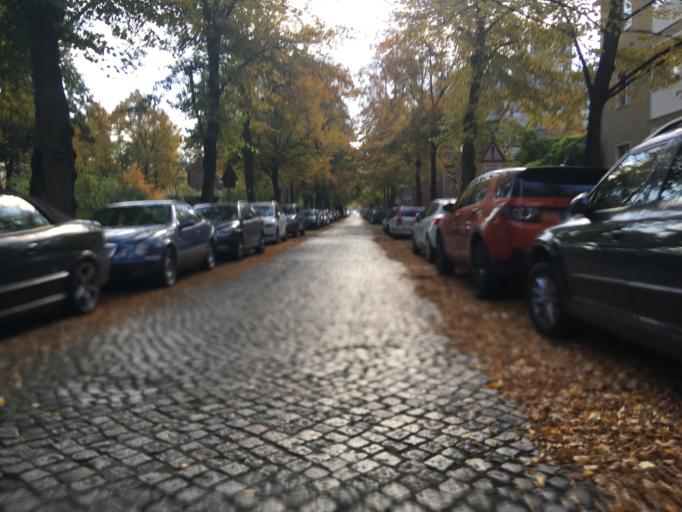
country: DE
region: Berlin
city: Wedding Bezirk
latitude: 52.5650
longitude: 13.3541
